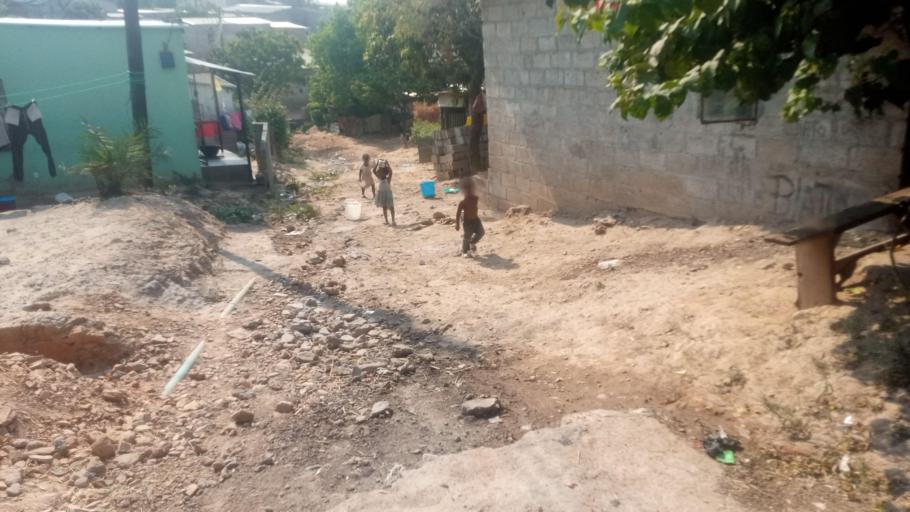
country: ZM
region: Lusaka
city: Lusaka
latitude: -15.4427
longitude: 28.3882
